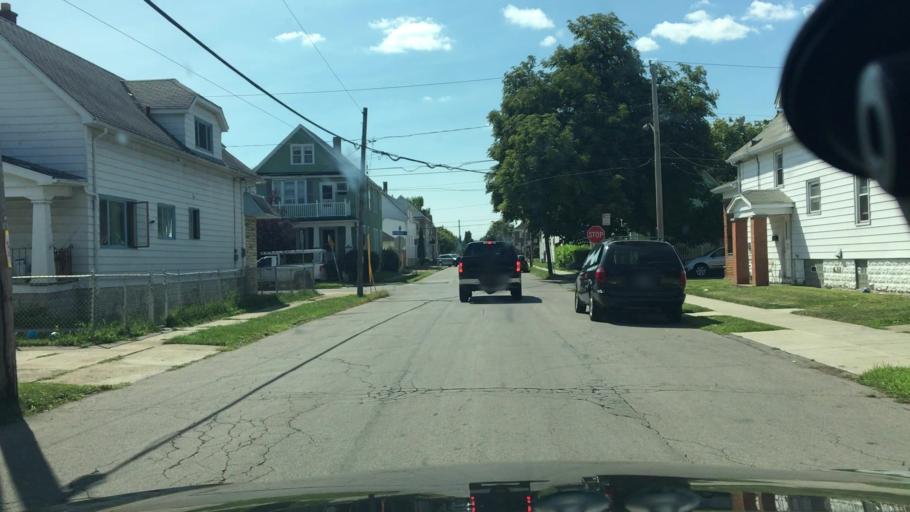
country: US
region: New York
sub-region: Erie County
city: West Seneca
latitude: 42.8687
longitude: -78.8054
